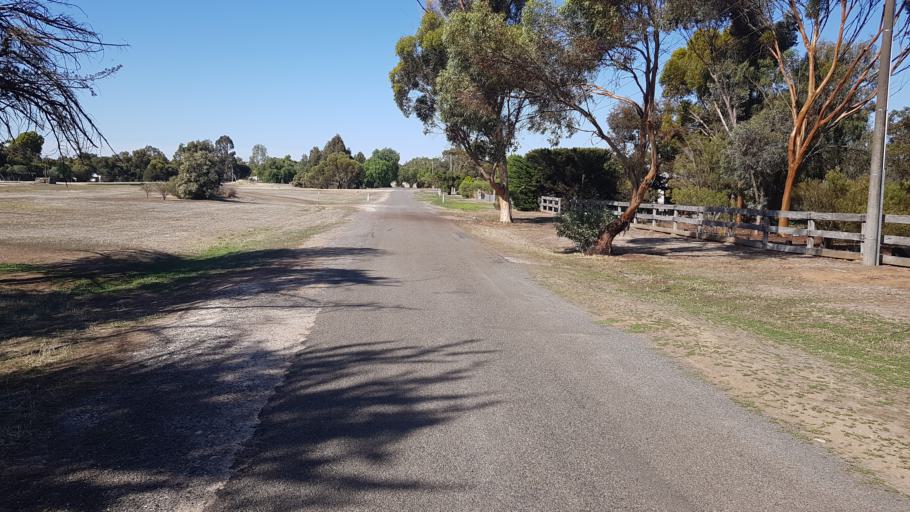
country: AU
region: Victoria
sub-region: Horsham
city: Horsham
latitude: -36.7453
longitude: 141.9403
